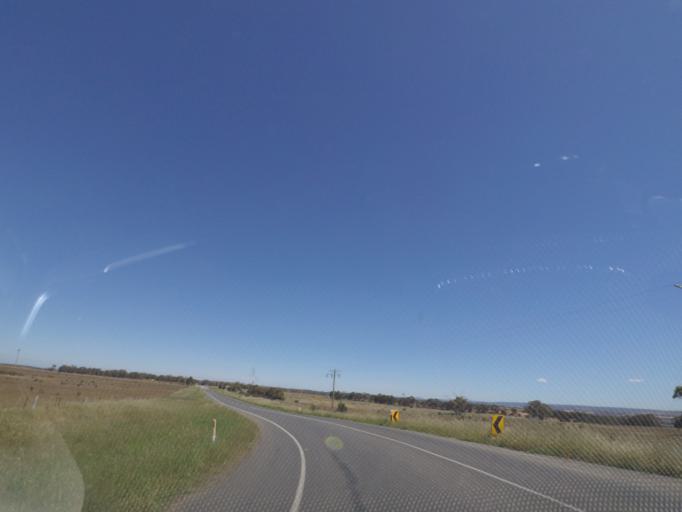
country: AU
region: Victoria
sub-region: Melton
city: Brookfield
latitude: -37.6818
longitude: 144.5036
